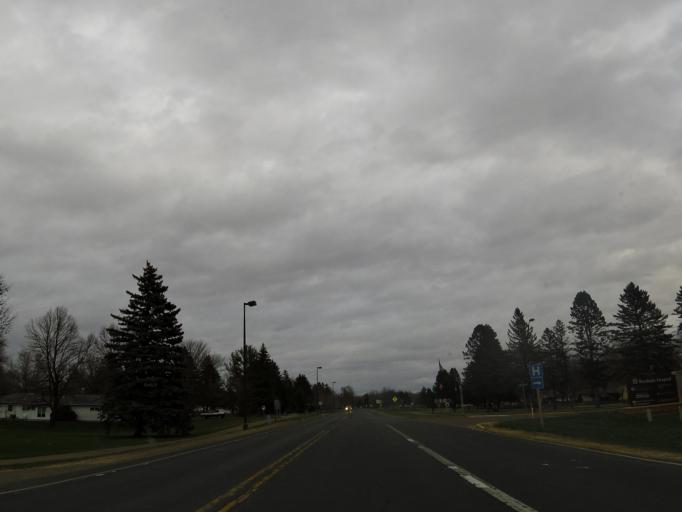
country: US
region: Wisconsin
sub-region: Saint Croix County
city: New Richmond
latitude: 45.1188
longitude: -92.5540
